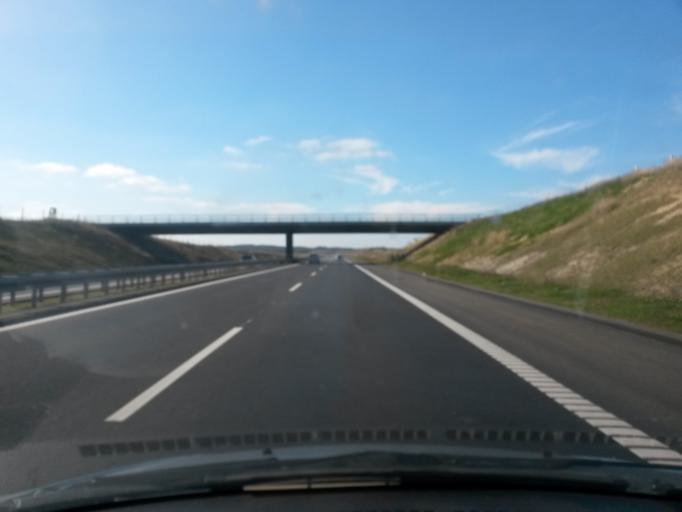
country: DK
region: Central Jutland
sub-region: Skanderborg Kommune
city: Ry
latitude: 56.1486
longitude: 9.7298
